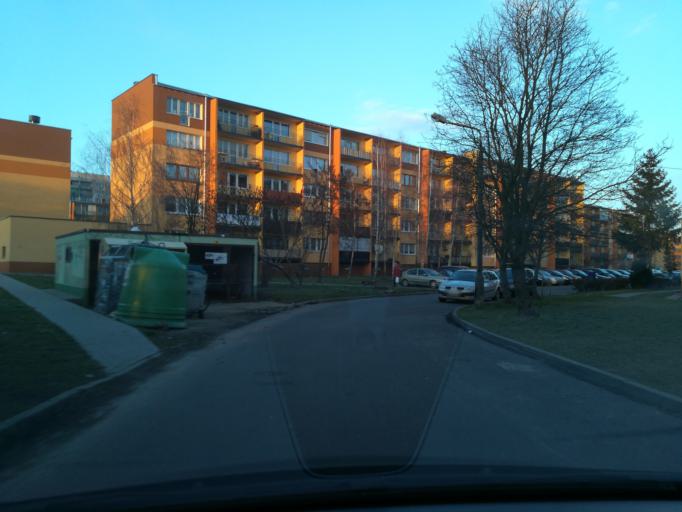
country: PL
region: Lodz Voivodeship
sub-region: Piotrkow Trybunalski
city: Piotrkow Trybunalski
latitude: 51.4080
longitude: 19.6585
